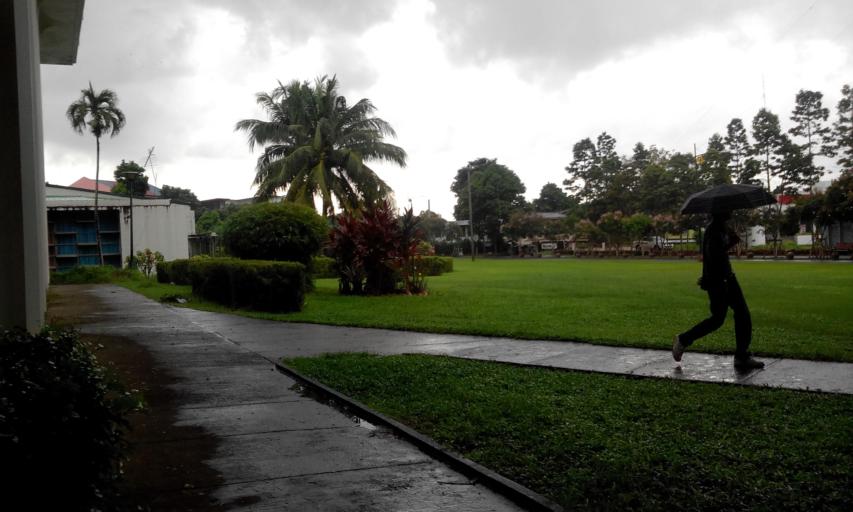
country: PH
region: Calabarzon
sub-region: Province of Laguna
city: Los Banos
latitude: 14.1672
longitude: 121.2428
